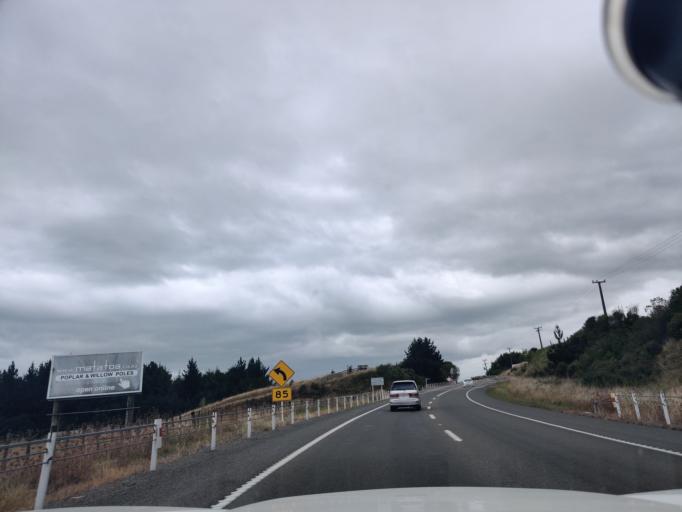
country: NZ
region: Manawatu-Wanganui
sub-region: Horowhenua District
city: Foxton
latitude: -40.5589
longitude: 175.4060
